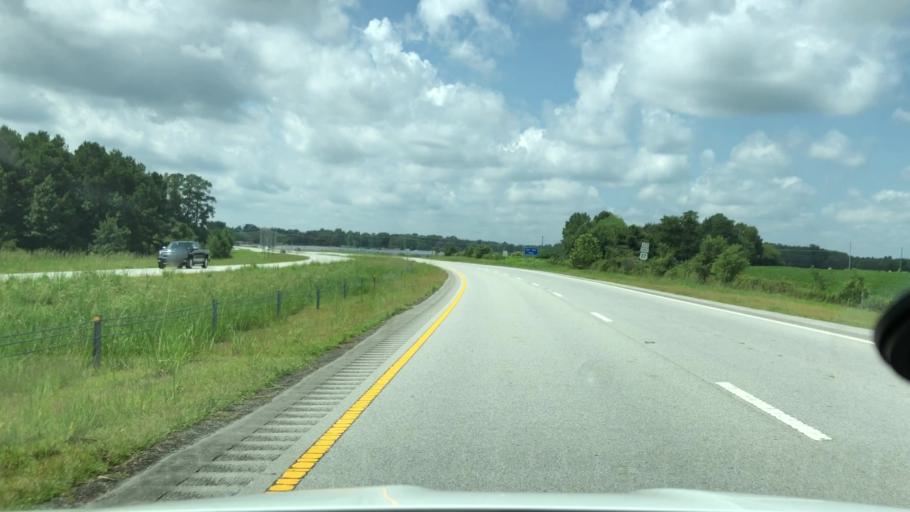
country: US
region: North Carolina
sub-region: Beaufort County
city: Washington
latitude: 35.5029
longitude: -77.0996
